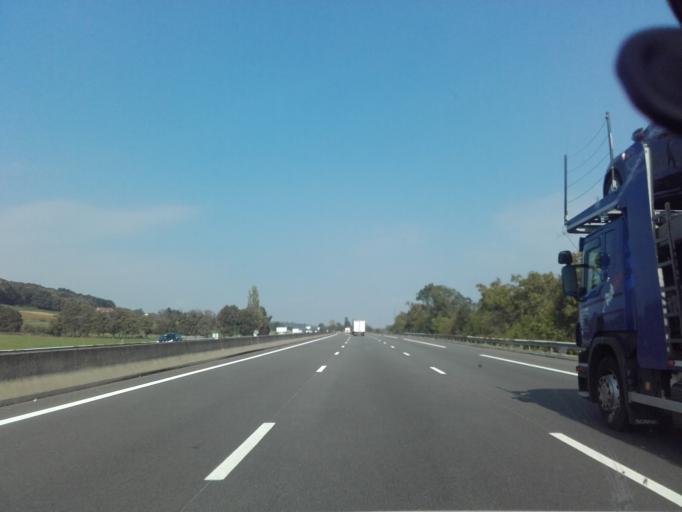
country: FR
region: Bourgogne
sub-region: Departement de Saone-et-Loire
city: Saint-Martin-Belle-Roche
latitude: 46.3874
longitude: 4.8513
